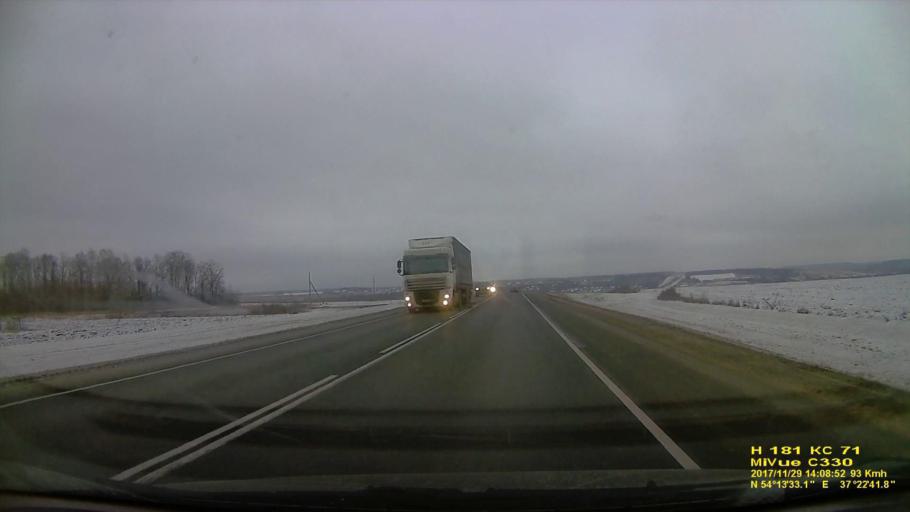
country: RU
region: Tula
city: Leninskiy
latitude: 54.2256
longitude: 37.3788
